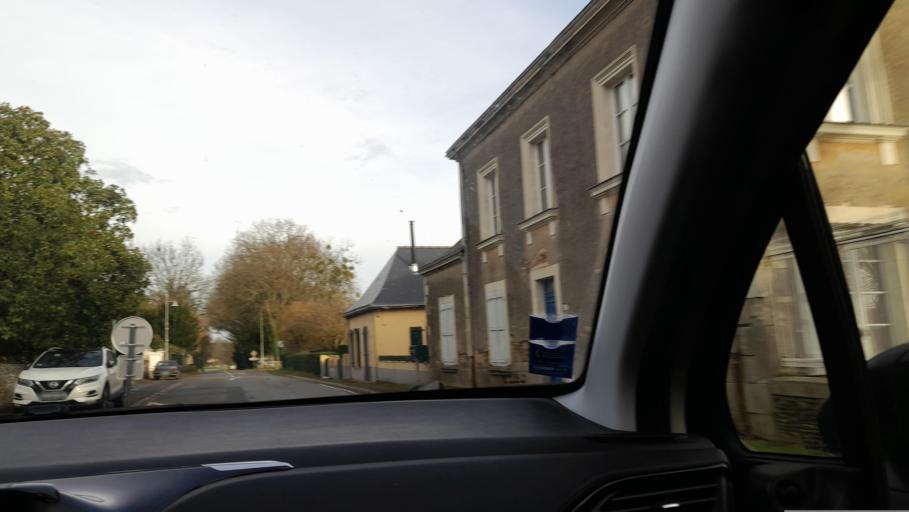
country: FR
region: Pays de la Loire
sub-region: Departement de la Mayenne
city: Ballots
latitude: 47.8971
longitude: -1.1108
